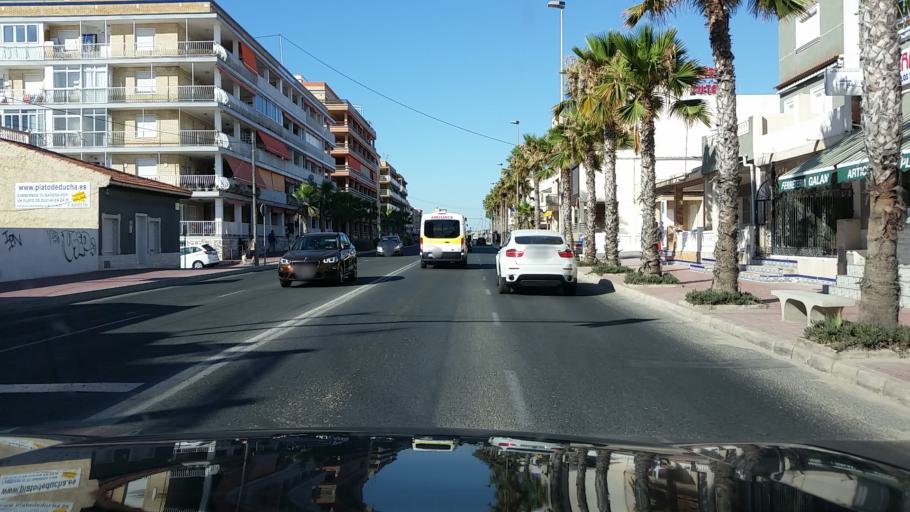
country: ES
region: Valencia
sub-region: Provincia de Alicante
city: Torrevieja
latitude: 37.9692
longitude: -0.6975
